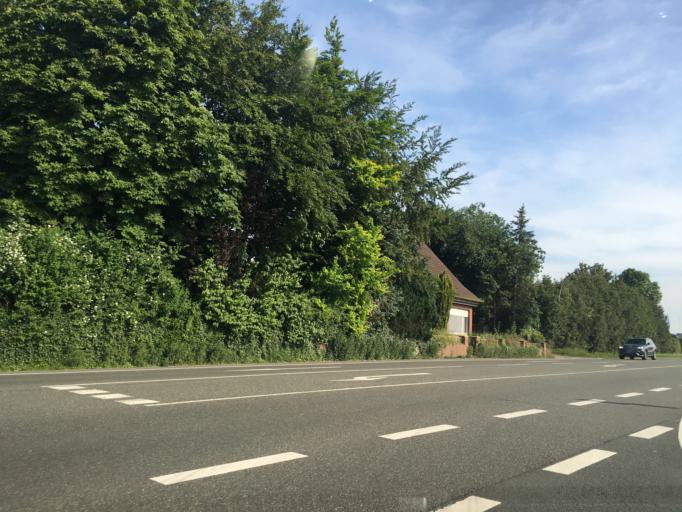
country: DE
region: North Rhine-Westphalia
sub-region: Regierungsbezirk Munster
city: Steinfurt
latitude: 52.1577
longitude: 7.3424
